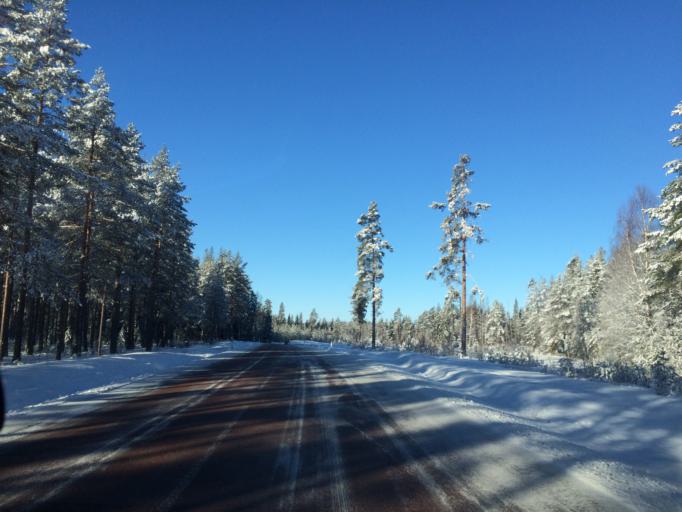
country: SE
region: Dalarna
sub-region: Mora Kommun
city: Mora
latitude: 60.8475
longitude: 14.2775
